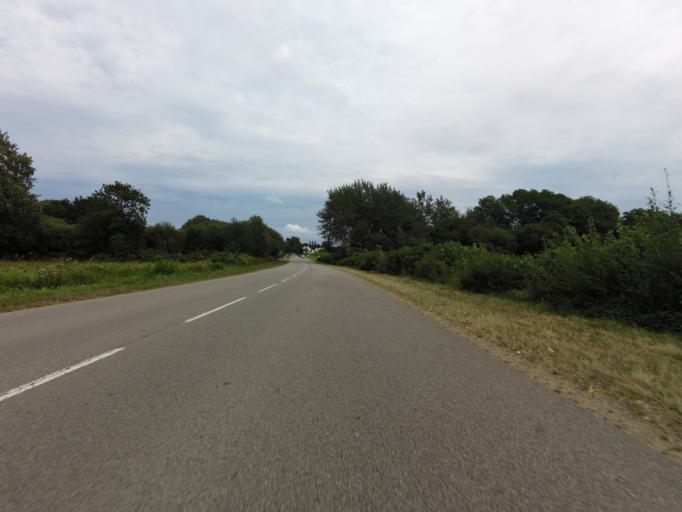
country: FR
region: Brittany
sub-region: Departement du Finistere
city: Poullan-sur-Mer
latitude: 48.0839
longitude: -4.3794
